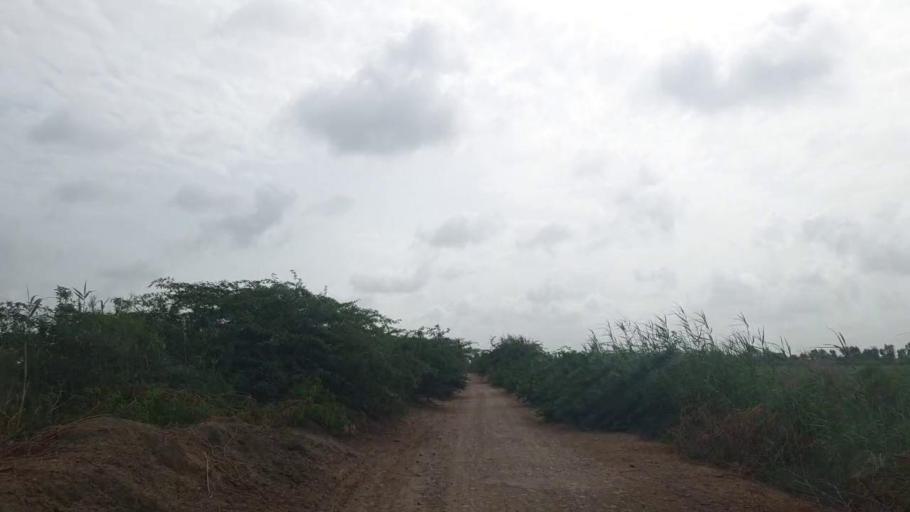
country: PK
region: Sindh
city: Tando Bago
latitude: 24.8095
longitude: 69.0281
